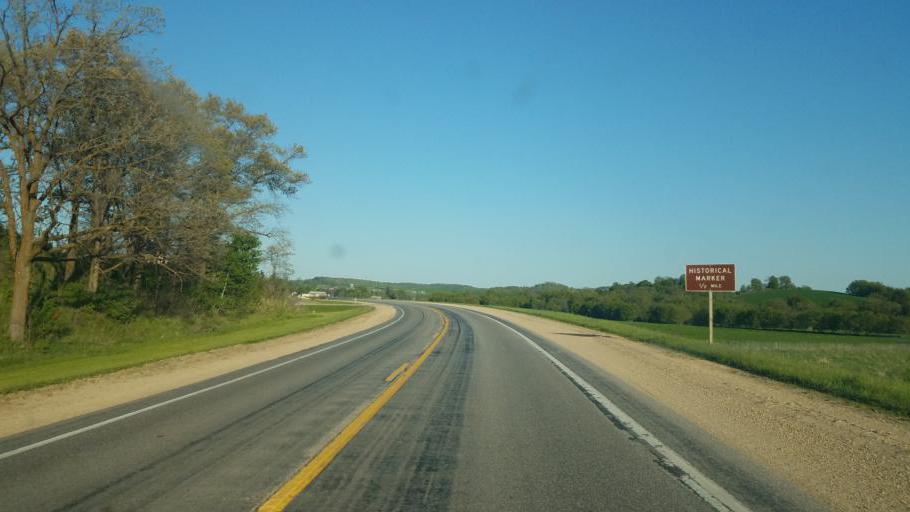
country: US
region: Wisconsin
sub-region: Vernon County
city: Hillsboro
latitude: 43.6546
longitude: -90.3634
